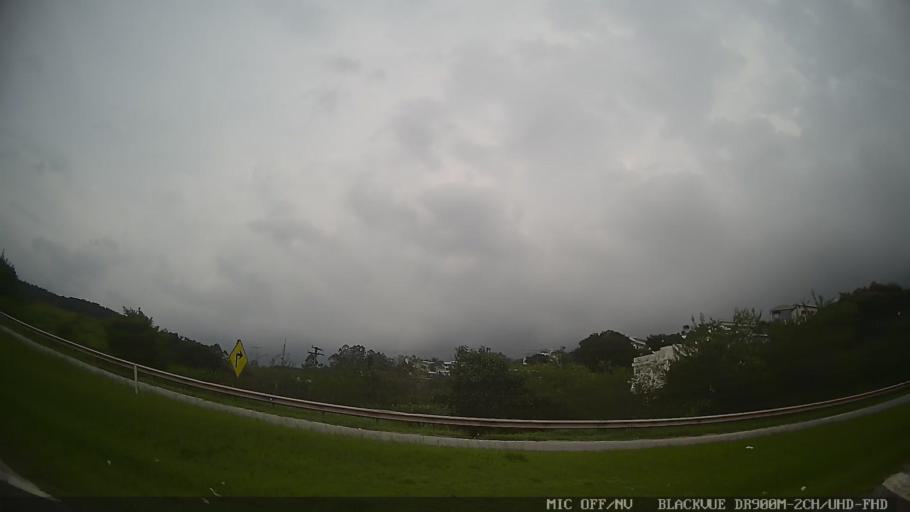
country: BR
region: Sao Paulo
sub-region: Aruja
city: Aruja
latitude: -23.4381
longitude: -46.2611
